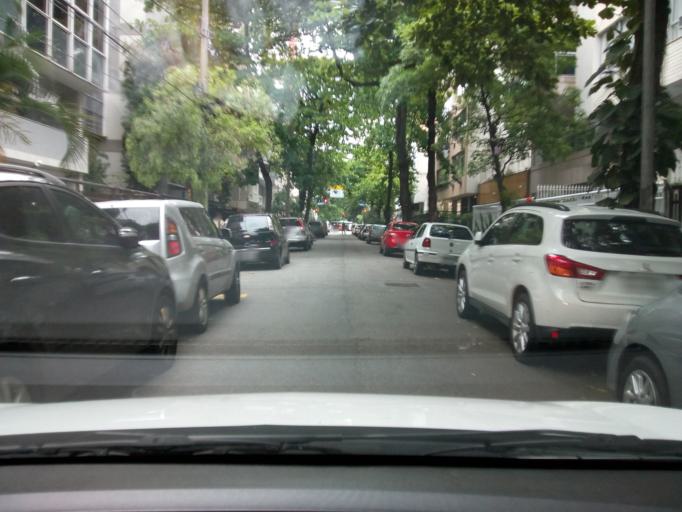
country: BR
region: Rio de Janeiro
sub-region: Rio De Janeiro
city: Rio de Janeiro
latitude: -22.9830
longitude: -43.2226
